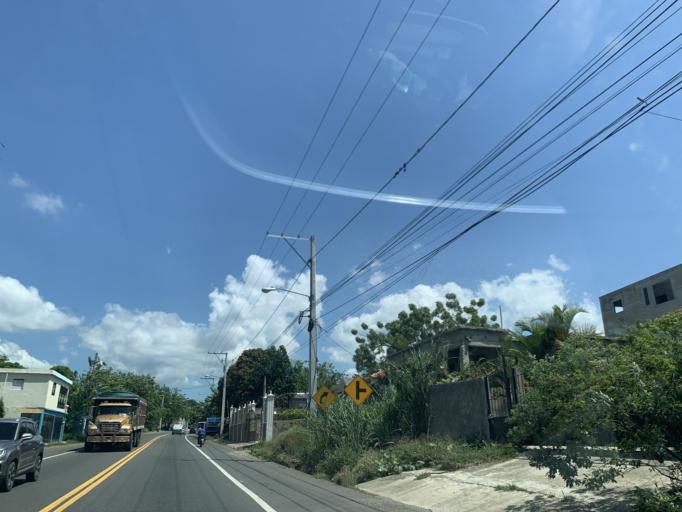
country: DO
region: Puerto Plata
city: Imbert
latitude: 19.7300
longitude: -70.8293
